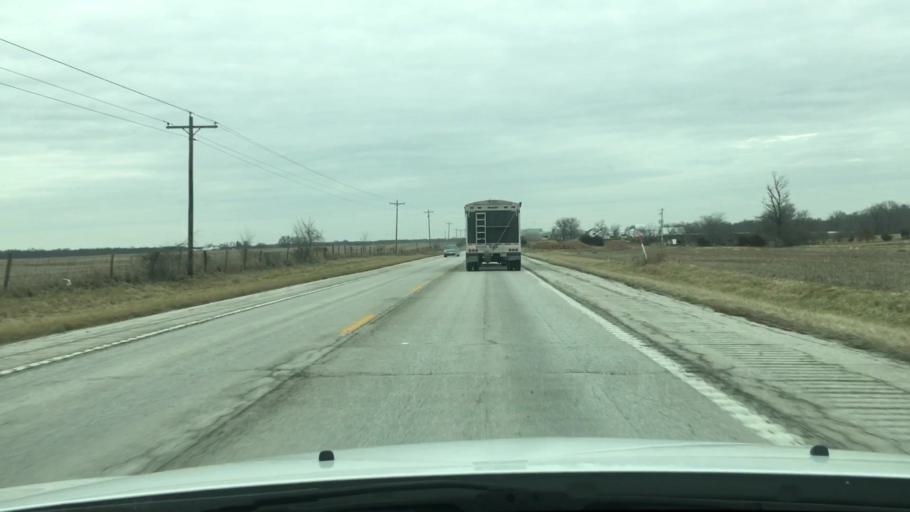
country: US
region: Missouri
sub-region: Montgomery County
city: Wellsville
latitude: 39.1718
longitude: -91.6477
